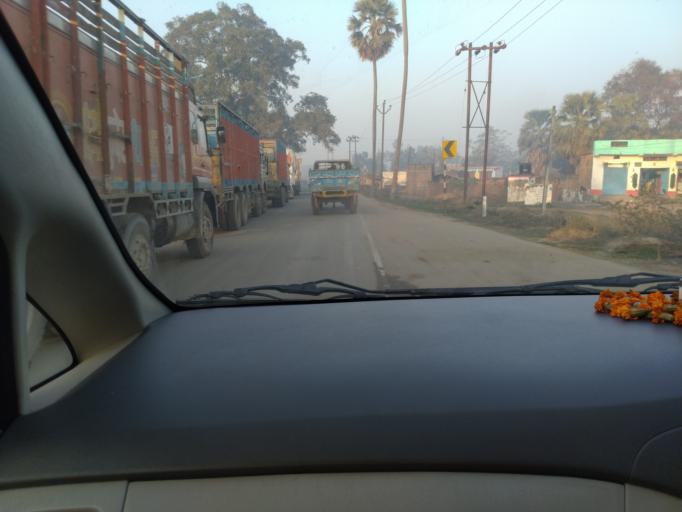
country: IN
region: Bihar
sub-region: Patna
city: Khagaul
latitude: 25.4816
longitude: 84.9317
